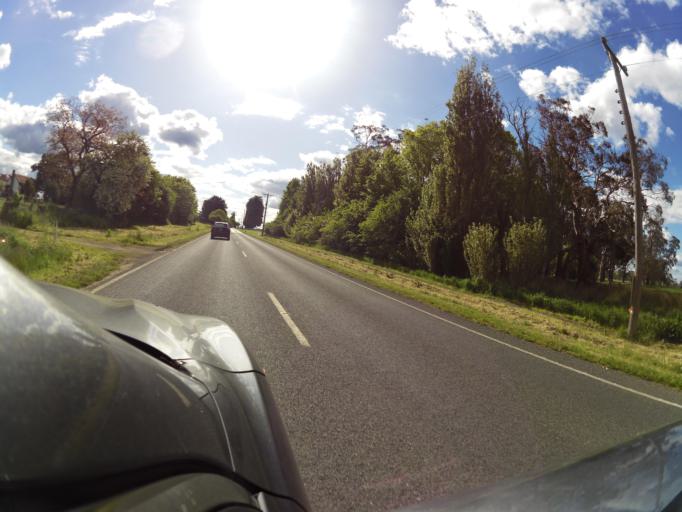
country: AU
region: Victoria
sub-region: Mount Alexander
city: Castlemaine
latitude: -37.3427
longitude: 144.1733
